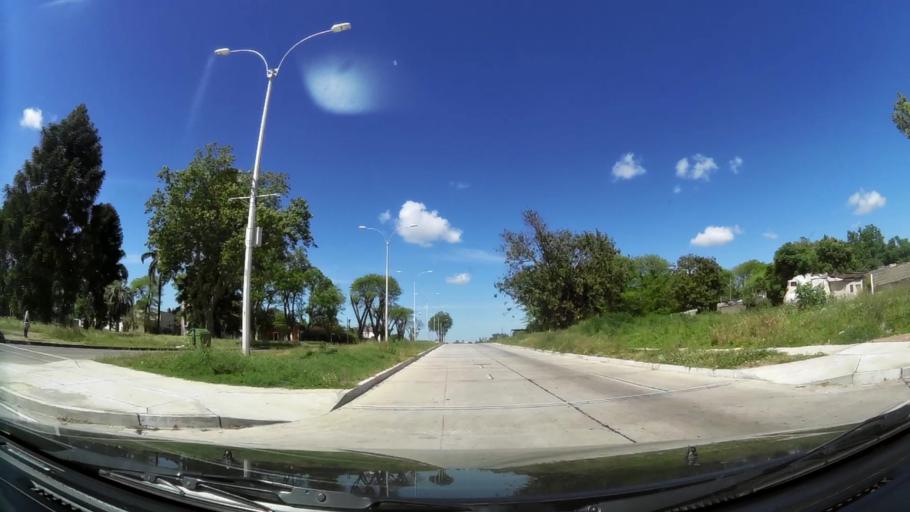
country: UY
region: Montevideo
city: Montevideo
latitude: -34.8455
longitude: -56.1451
